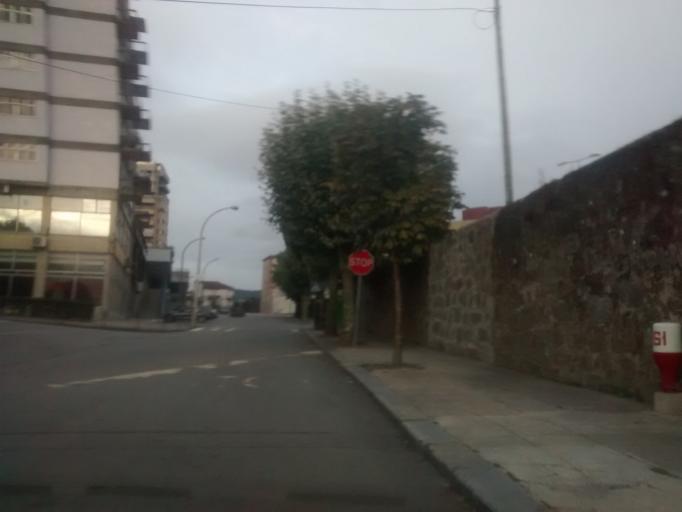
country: PT
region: Braga
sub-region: Braga
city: Braga
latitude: 41.5448
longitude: -8.4354
